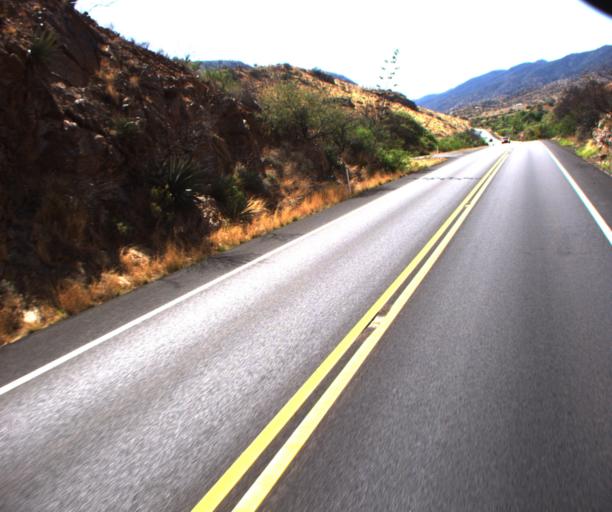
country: US
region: Arizona
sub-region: Cochise County
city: Bisbee
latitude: 31.5045
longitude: -110.0075
